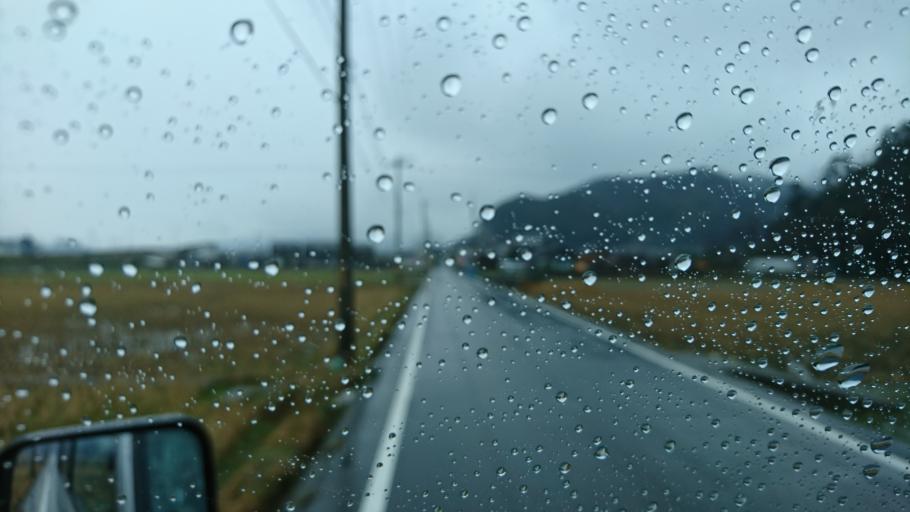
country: JP
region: Tottori
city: Tottori
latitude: 35.6073
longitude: 134.4759
